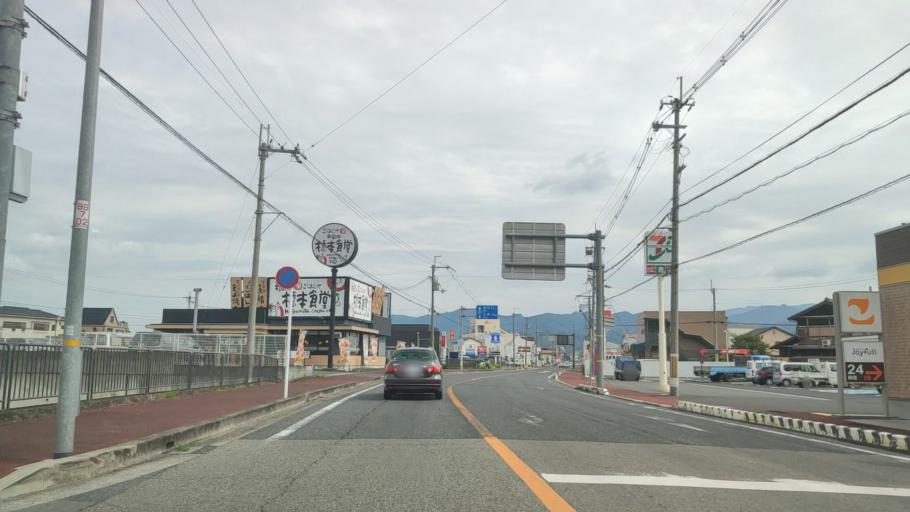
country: JP
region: Wakayama
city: Hashimoto
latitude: 34.3057
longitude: 135.5461
